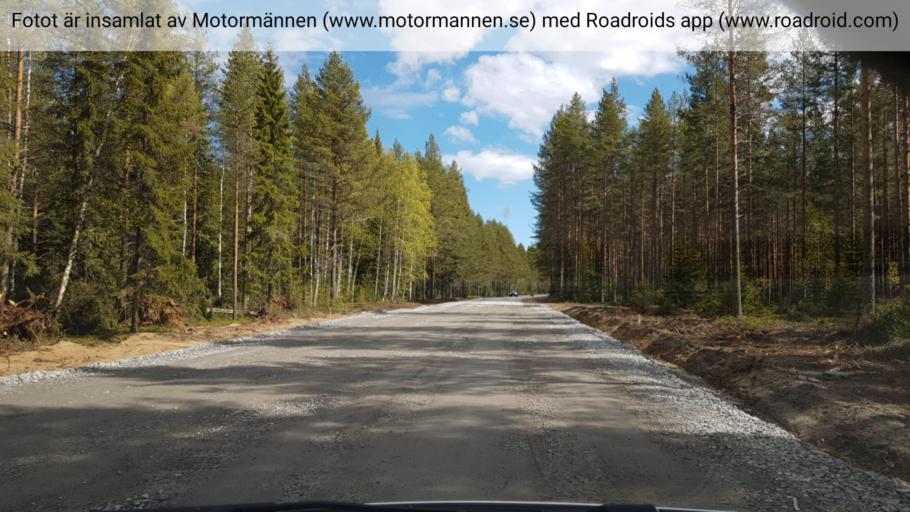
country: SE
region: Vaesterbotten
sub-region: Vindelns Kommun
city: Vindeln
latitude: 64.1735
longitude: 19.7443
